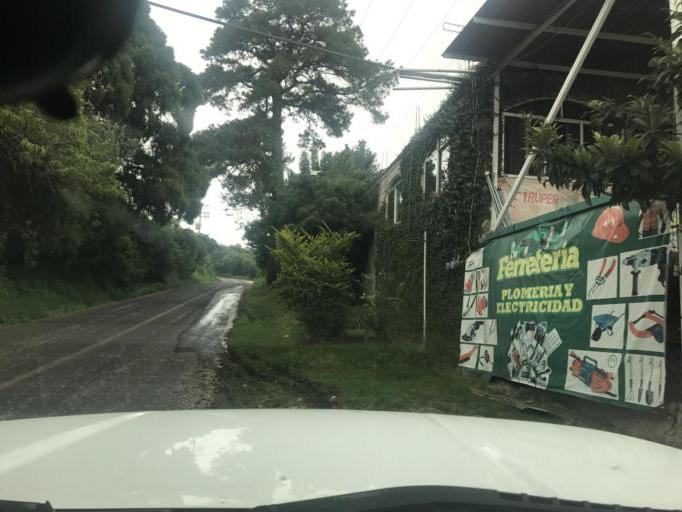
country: MX
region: Morelos
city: Ocuituco
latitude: 18.8817
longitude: -98.7628
